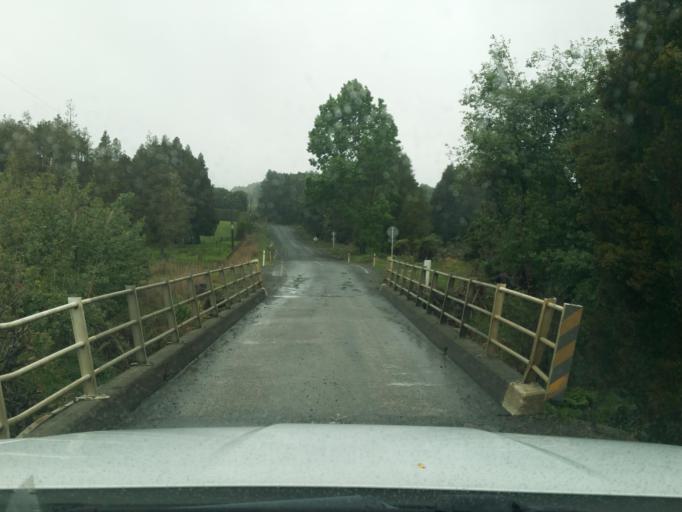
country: NZ
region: Northland
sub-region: Kaipara District
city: Dargaville
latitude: -35.7411
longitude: 173.9080
